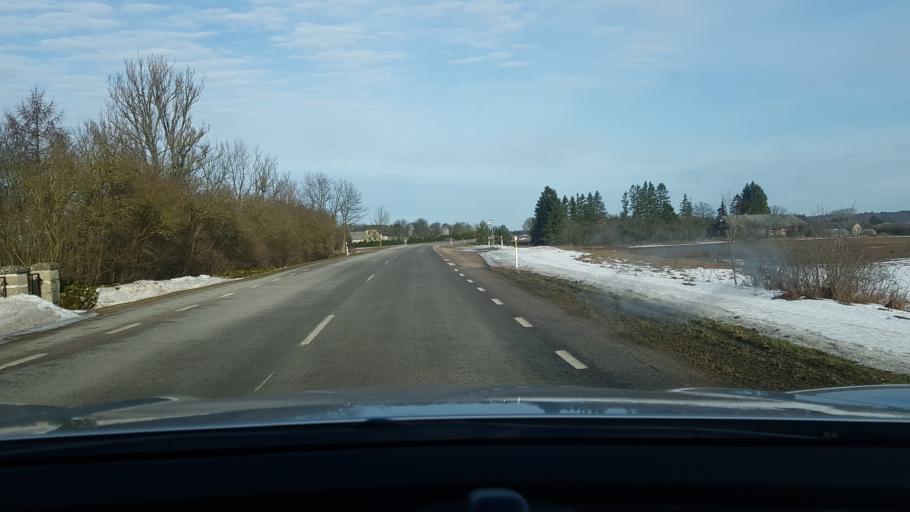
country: EE
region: Saare
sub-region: Kuressaare linn
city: Kuressaare
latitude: 58.5217
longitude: 22.7018
